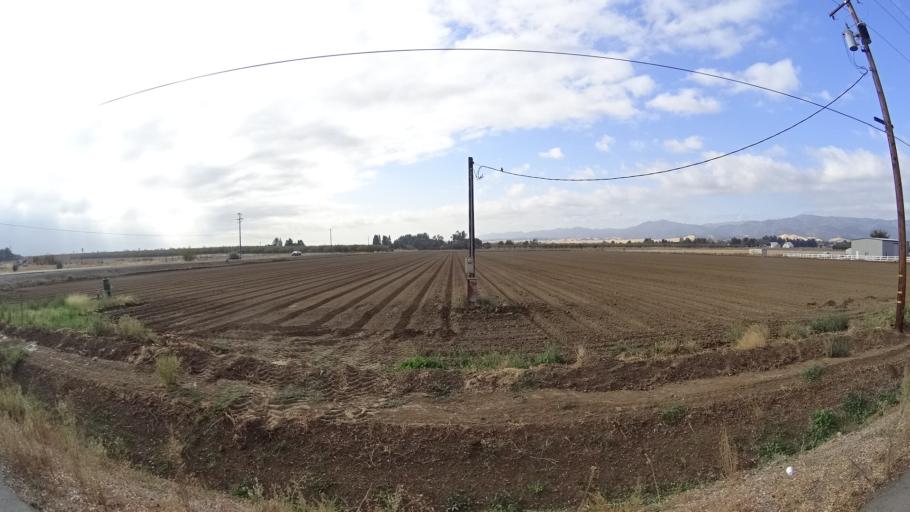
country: US
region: California
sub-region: Yolo County
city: Esparto
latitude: 38.6897
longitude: -122.0216
